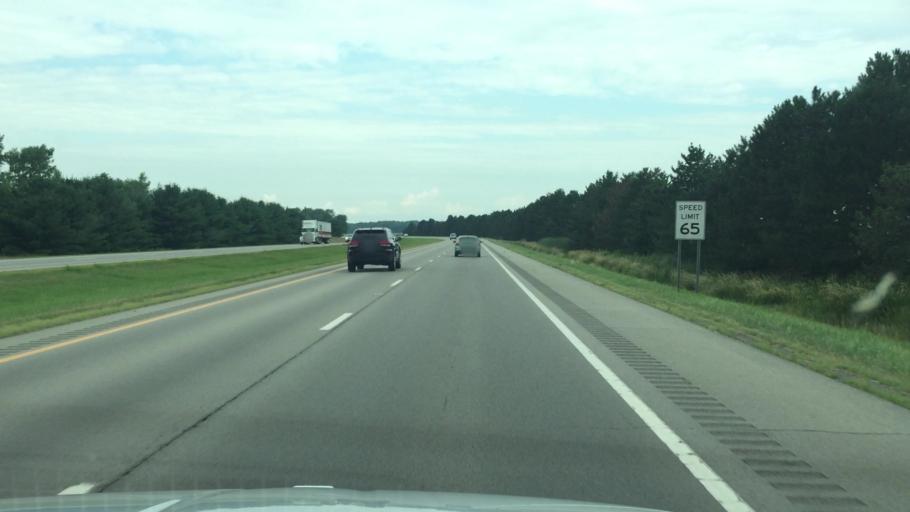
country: US
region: Ohio
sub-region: Wyandot County
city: Carey
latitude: 40.9770
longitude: -83.4923
